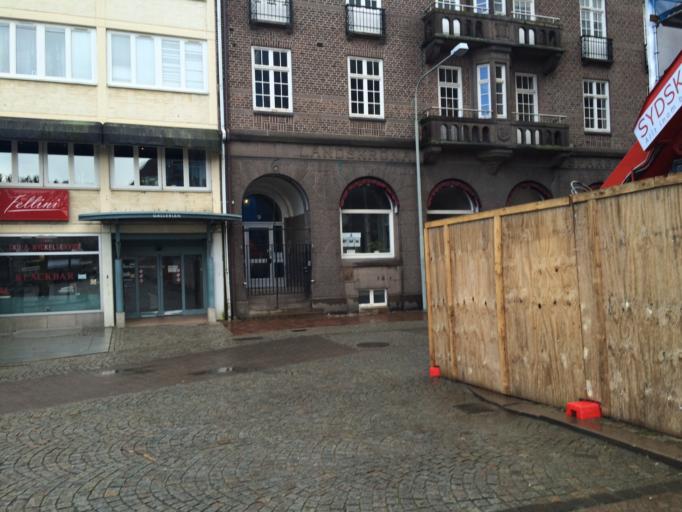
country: SE
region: Skane
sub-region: Landskrona
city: Landskrona
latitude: 55.8702
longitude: 12.8305
